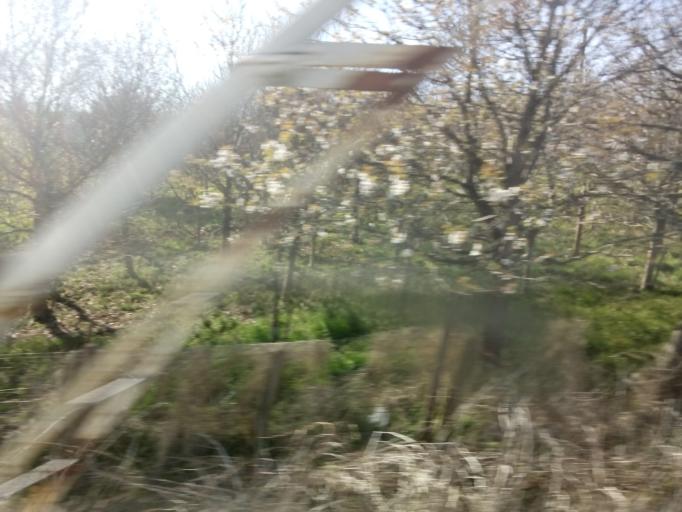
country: GB
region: Scotland
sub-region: East Lothian
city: Dunbar
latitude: 55.9917
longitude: -2.5548
